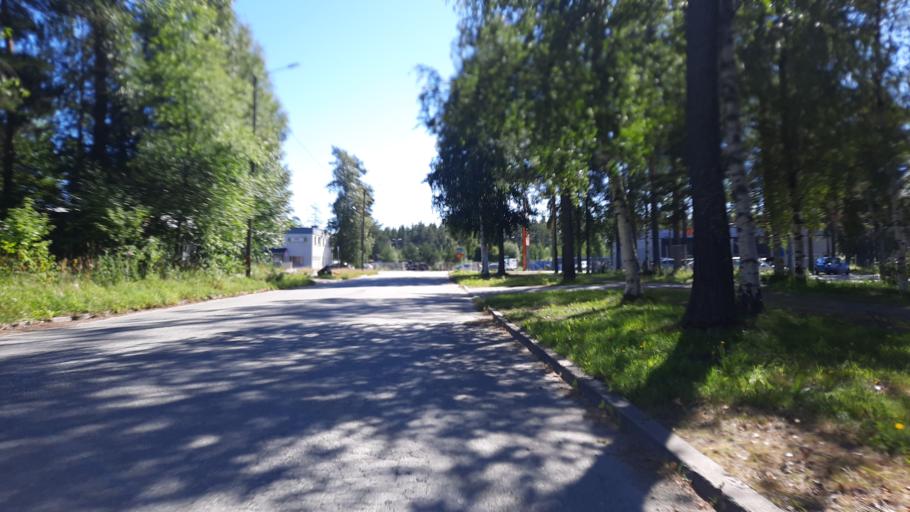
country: FI
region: North Karelia
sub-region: Joensuu
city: Joensuu
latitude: 62.6190
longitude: 29.7625
